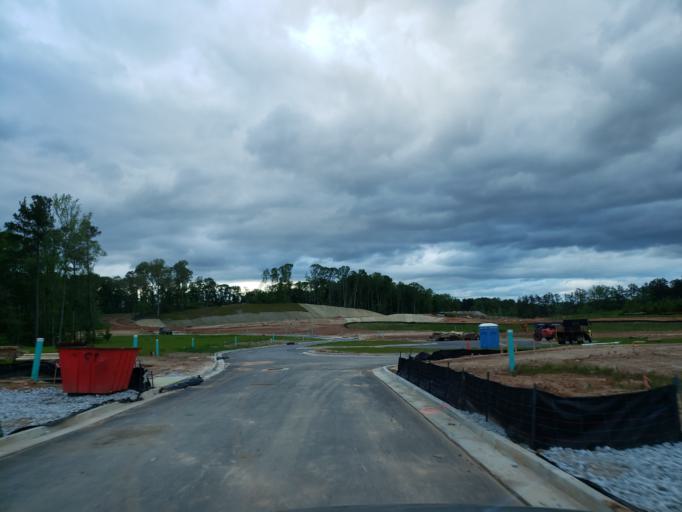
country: US
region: Georgia
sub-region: Paulding County
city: Hiram
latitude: 33.9059
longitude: -84.7323
